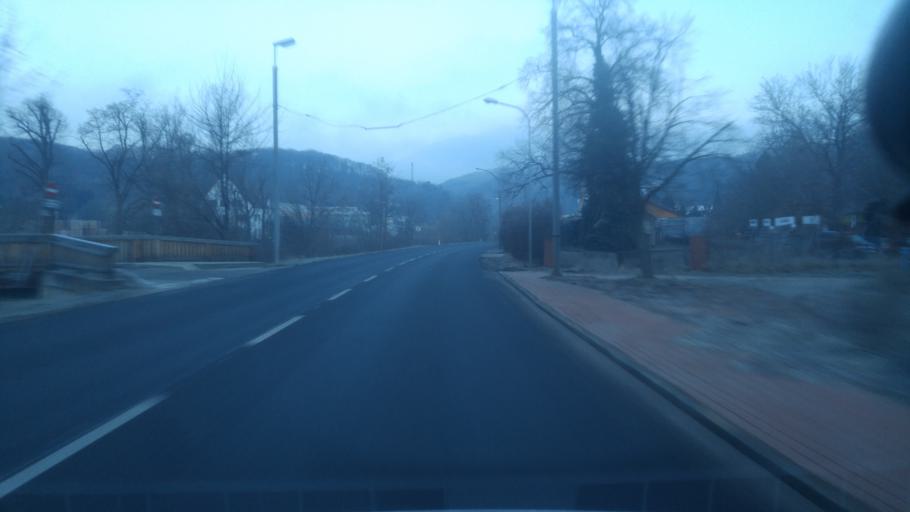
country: AT
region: Lower Austria
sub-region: Politischer Bezirk Baden
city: Pottenstein
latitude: 47.9619
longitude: 16.0904
